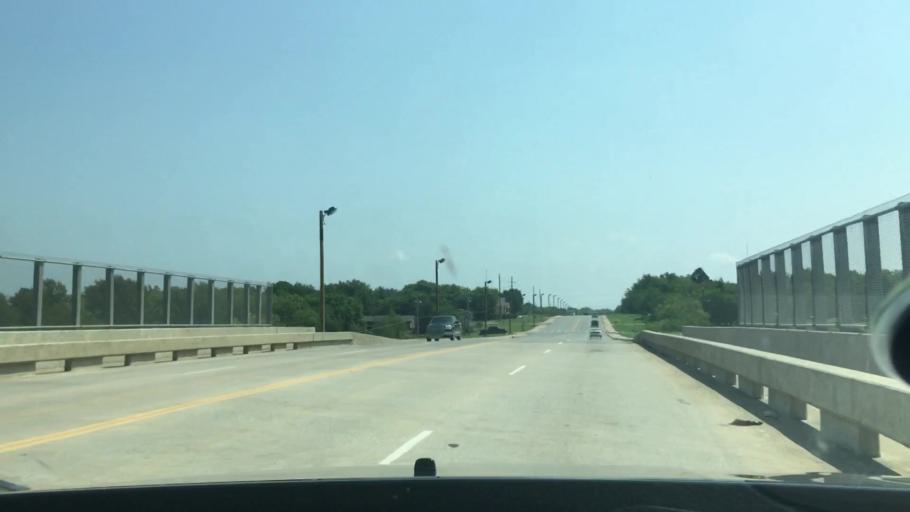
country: US
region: Oklahoma
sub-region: Atoka County
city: Atoka
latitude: 34.3747
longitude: -96.1302
